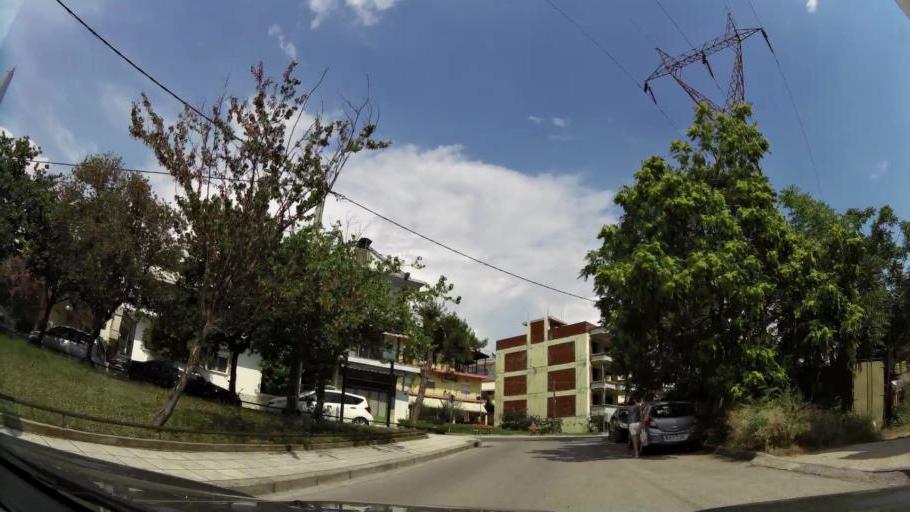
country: GR
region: Central Macedonia
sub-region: Nomos Thessalonikis
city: Stavroupoli
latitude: 40.6748
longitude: 22.9416
